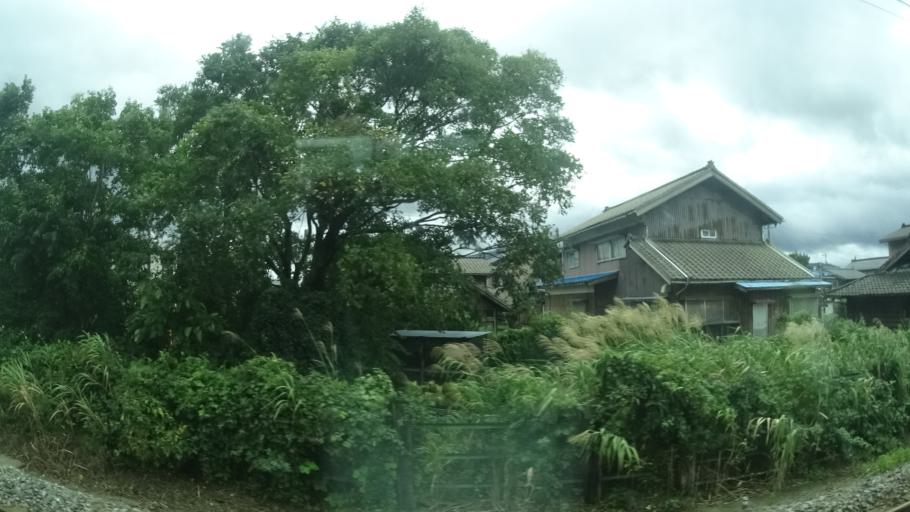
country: JP
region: Niigata
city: Murakami
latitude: 38.1170
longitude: 139.4439
